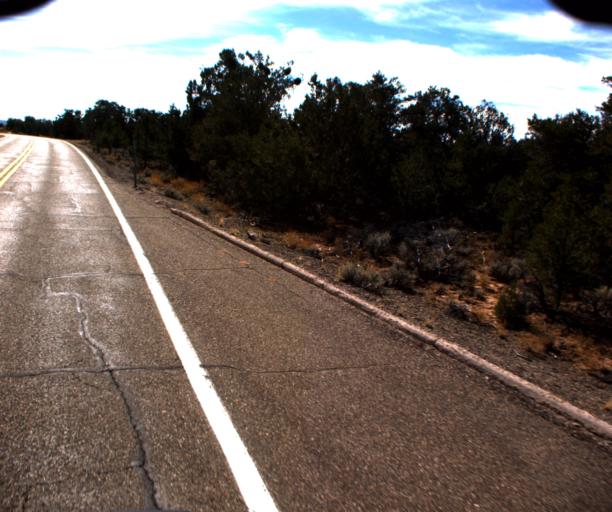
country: US
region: Arizona
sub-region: Navajo County
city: Kayenta
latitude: 36.6481
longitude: -110.5182
